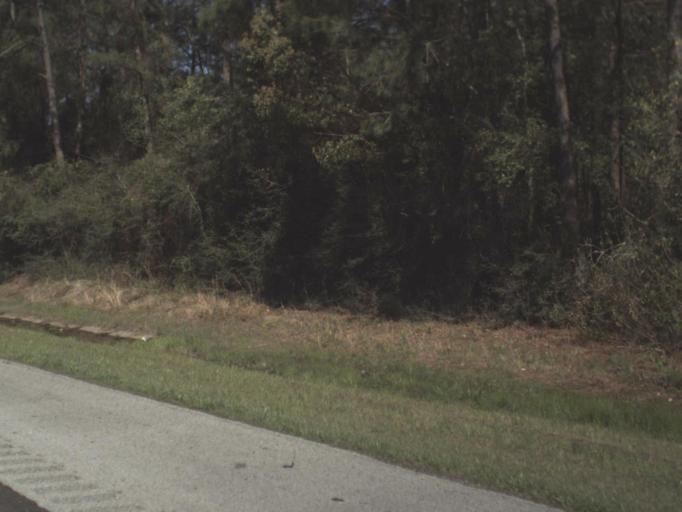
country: US
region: Florida
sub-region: Walton County
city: DeFuniak Springs
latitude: 30.6917
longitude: -86.1140
